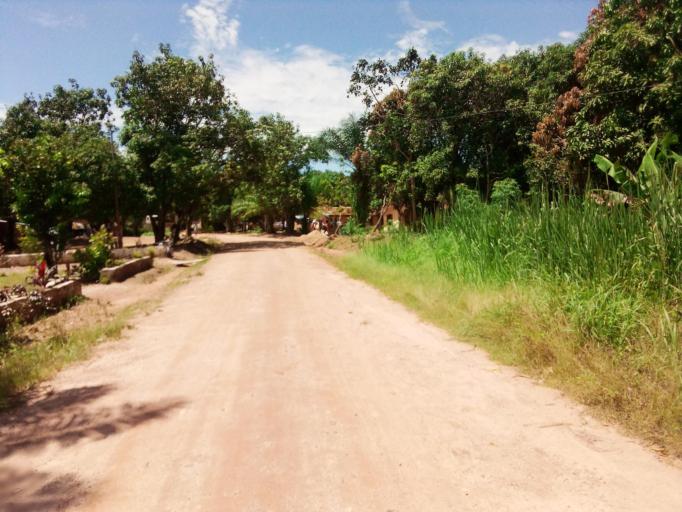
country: SL
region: Eastern Province
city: Koidu
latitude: 8.6515
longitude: -10.9471
